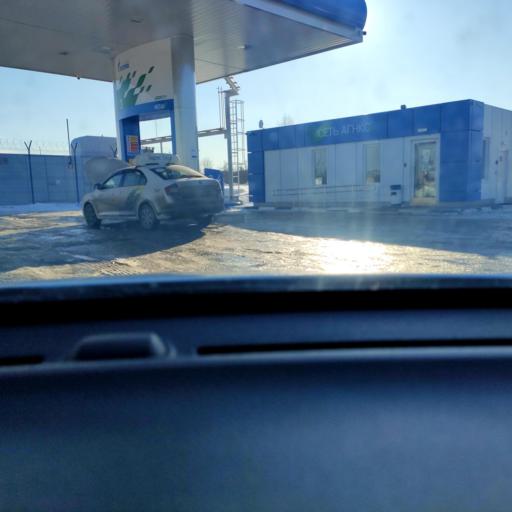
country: RU
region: Tatarstan
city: Osinovo
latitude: 55.8637
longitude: 48.8355
